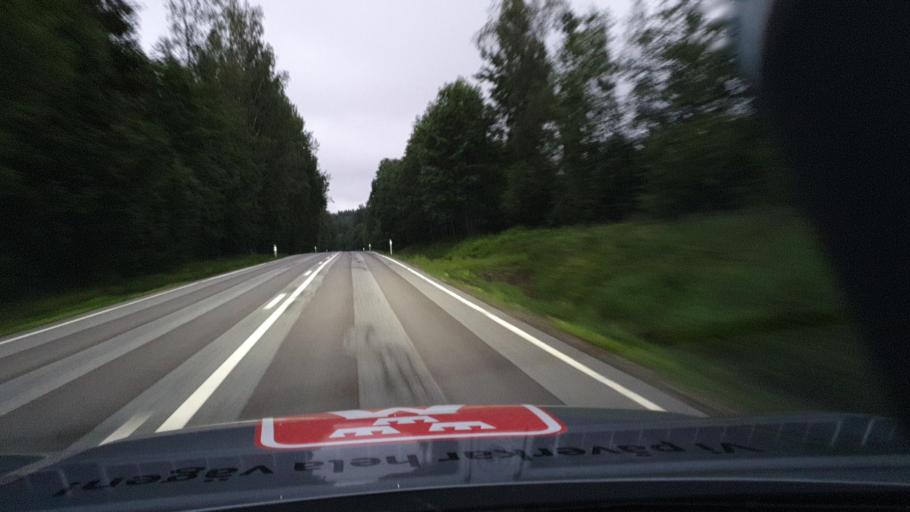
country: SE
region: OErebro
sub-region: Hallefors Kommun
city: Haellefors
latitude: 59.7532
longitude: 14.4398
